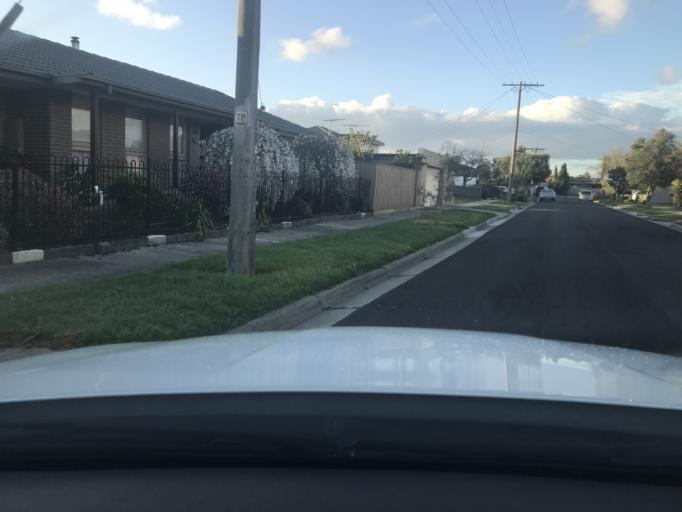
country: AU
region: Victoria
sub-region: Hume
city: Craigieburn
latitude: -37.5948
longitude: 144.9302
